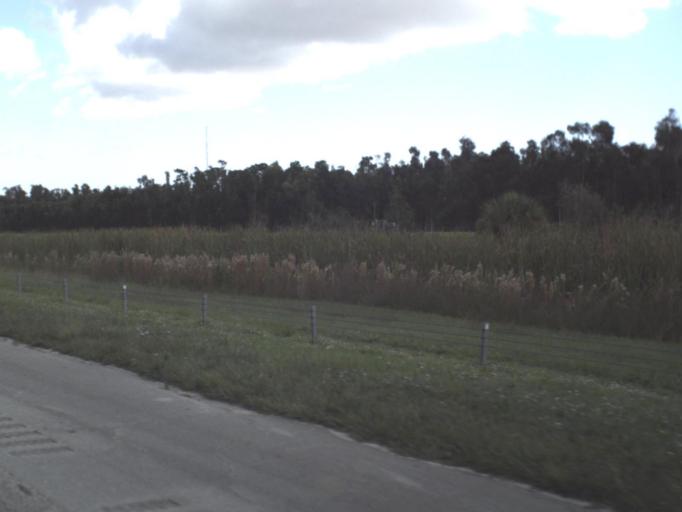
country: US
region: Florida
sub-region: Palm Beach County
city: Schall Circle
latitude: 26.7308
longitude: -80.1352
